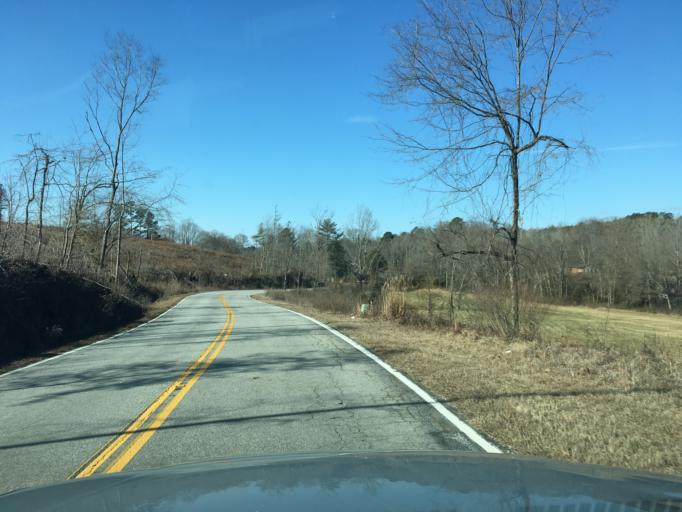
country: US
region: South Carolina
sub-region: Pickens County
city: Pickens
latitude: 34.8764
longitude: -82.6767
